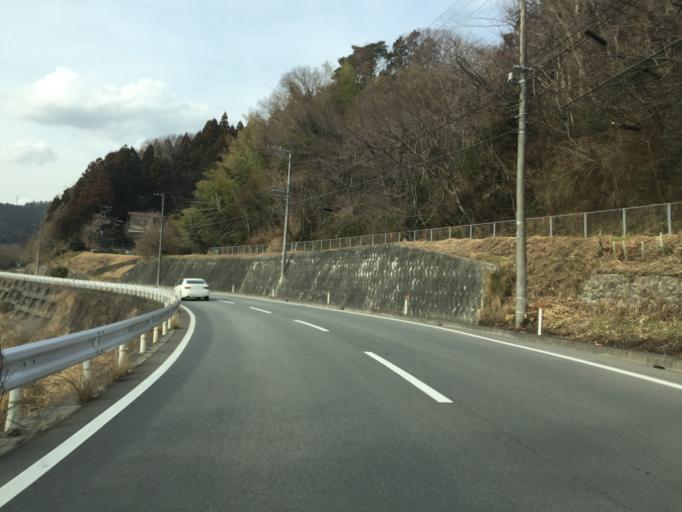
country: JP
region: Fukushima
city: Iwaki
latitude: 36.9974
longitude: 140.7309
